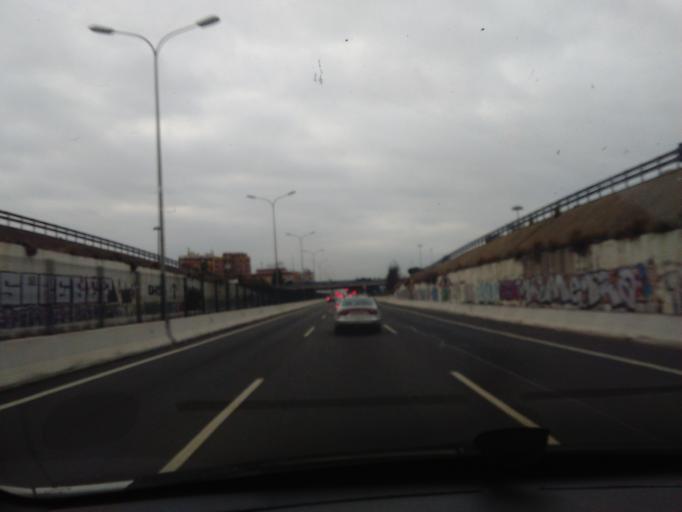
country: ES
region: Andalusia
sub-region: Provincia de Sevilla
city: Sevilla
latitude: 37.3863
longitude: -5.9377
